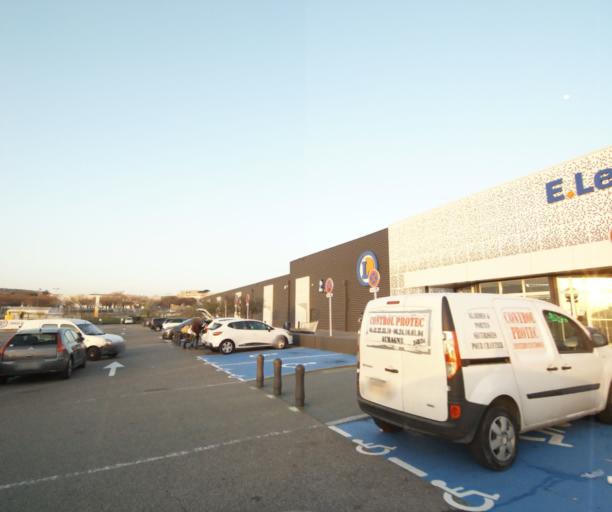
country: FR
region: Provence-Alpes-Cote d'Azur
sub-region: Departement des Bouches-du-Rhone
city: Saint-Victoret
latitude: 43.4248
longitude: 5.2704
